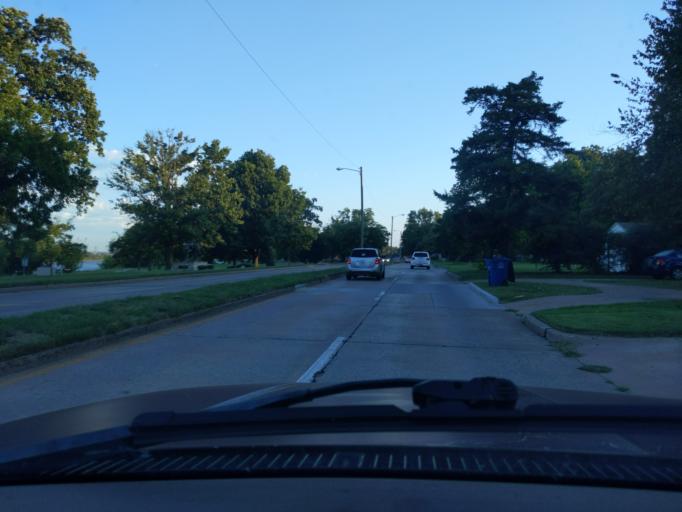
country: US
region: Oklahoma
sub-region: Tulsa County
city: Tulsa
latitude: 36.1008
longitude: -95.9840
